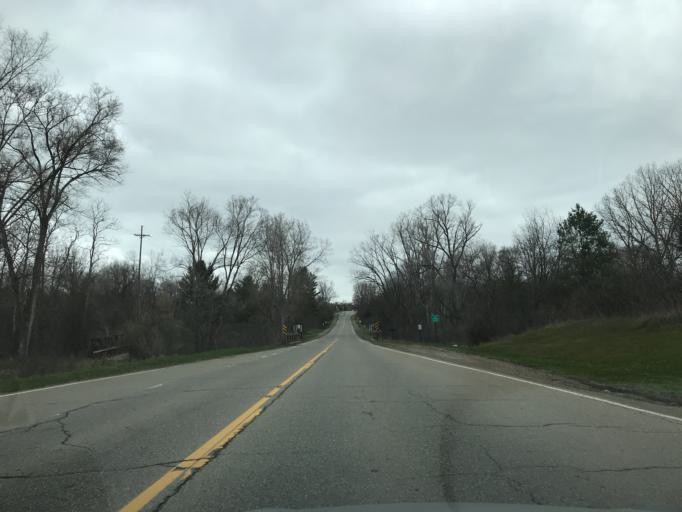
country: US
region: Michigan
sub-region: Oakland County
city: South Lyon
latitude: 42.5128
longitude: -83.6898
